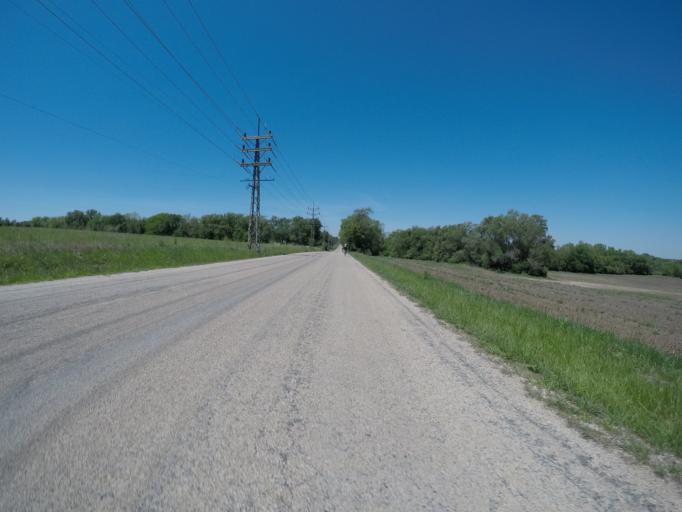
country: US
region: Kansas
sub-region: Shawnee County
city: Topeka
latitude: 39.0517
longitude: -95.6066
